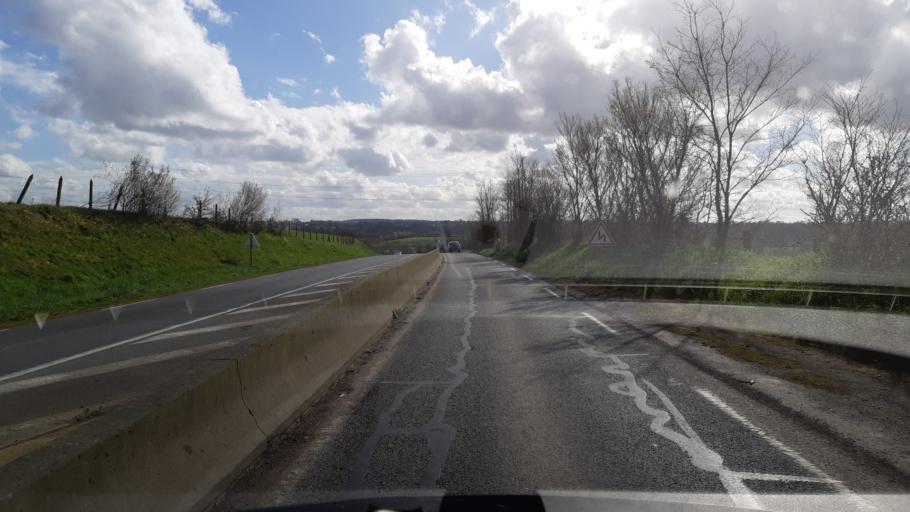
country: FR
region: Lower Normandy
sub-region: Departement de la Manche
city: Agneaux
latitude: 49.0984
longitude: -1.1200
